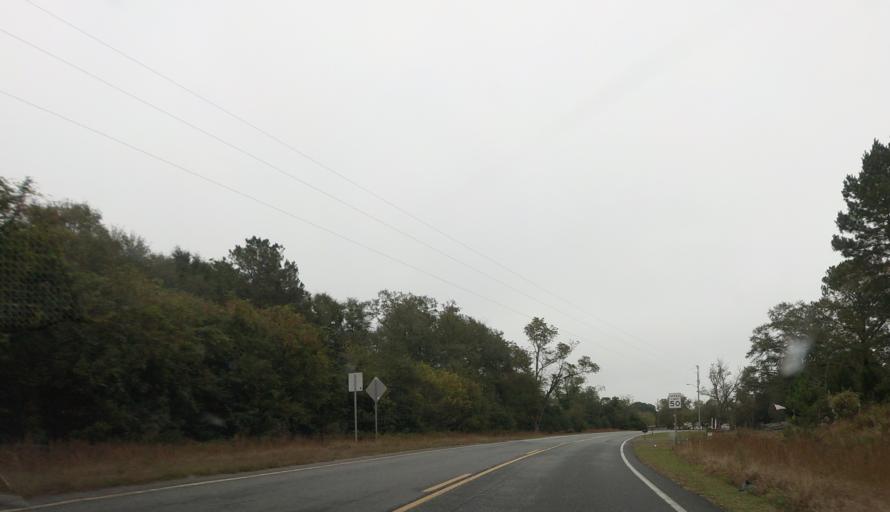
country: US
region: Georgia
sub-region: Marion County
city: Buena Vista
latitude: 32.3792
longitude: -84.4452
